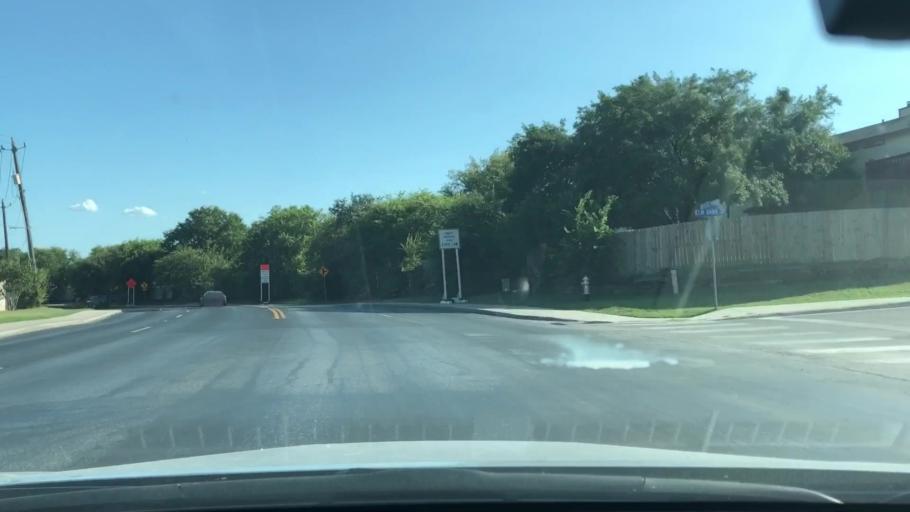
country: US
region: Texas
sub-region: Bexar County
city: Kirby
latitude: 29.4795
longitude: -98.3485
